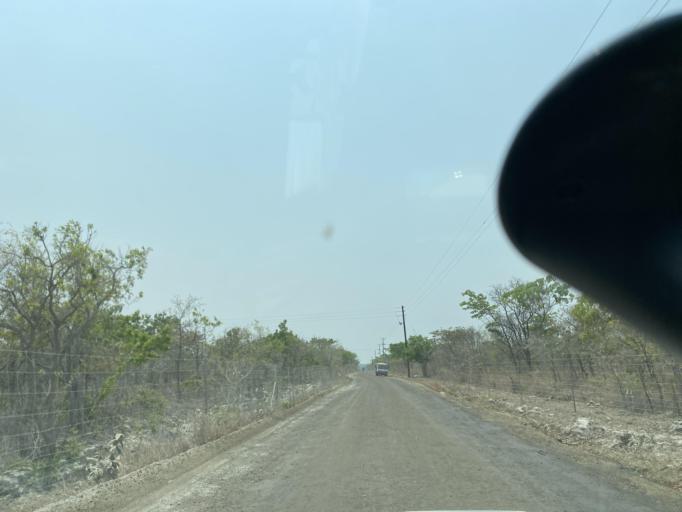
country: ZM
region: Lusaka
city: Lusaka
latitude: -15.5241
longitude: 28.4441
